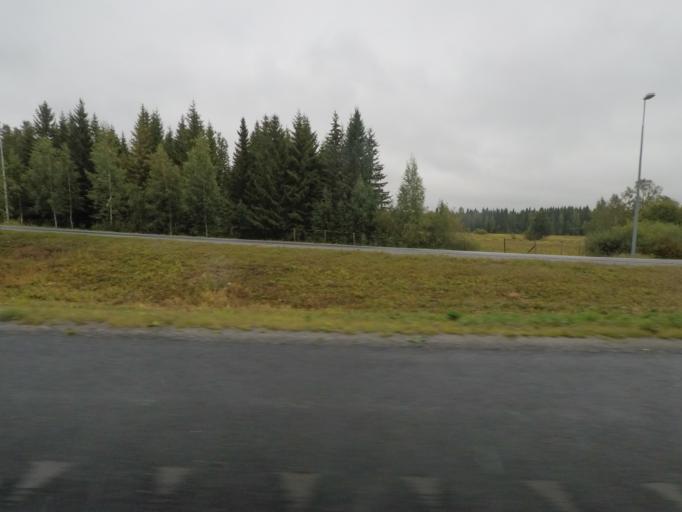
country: FI
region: Northern Savo
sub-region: Kuopio
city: Kuopio
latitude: 62.7965
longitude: 27.5946
